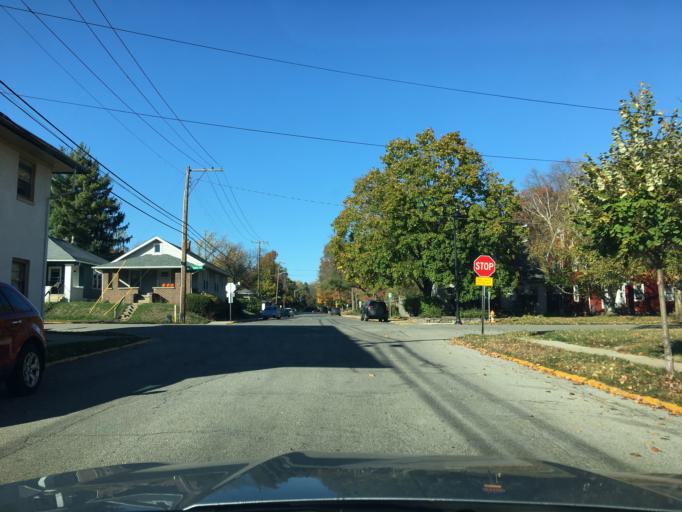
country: US
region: Indiana
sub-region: Tippecanoe County
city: West Lafayette
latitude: 40.4305
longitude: -86.9081
